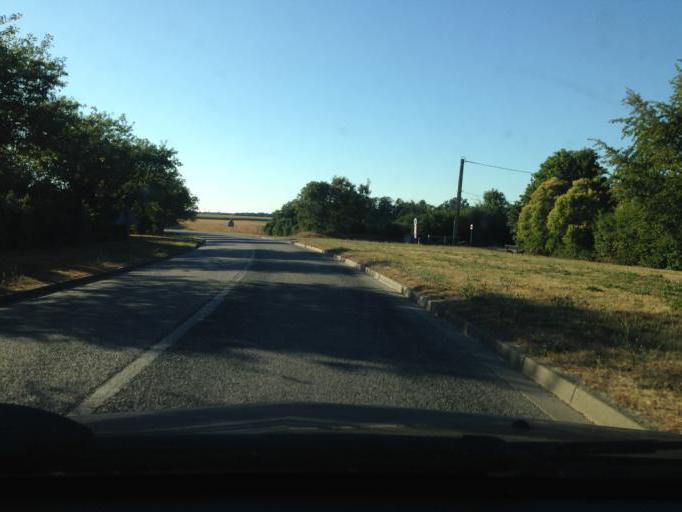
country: FR
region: Ile-de-France
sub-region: Departement des Yvelines
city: Chateaufort
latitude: 48.7296
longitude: 2.0808
